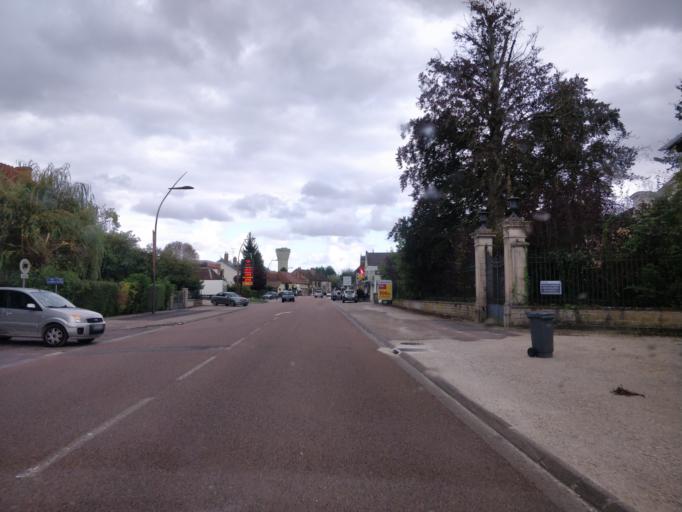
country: FR
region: Champagne-Ardenne
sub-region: Departement de l'Aube
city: Lusigny-sur-Barse
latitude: 48.2537
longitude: 4.2603
